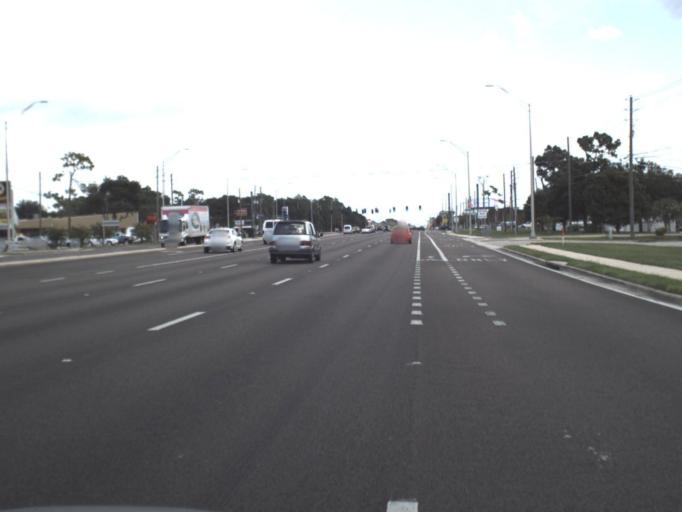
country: US
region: Florida
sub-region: Pinellas County
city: South Highpoint
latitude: 27.8938
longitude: -82.7033
